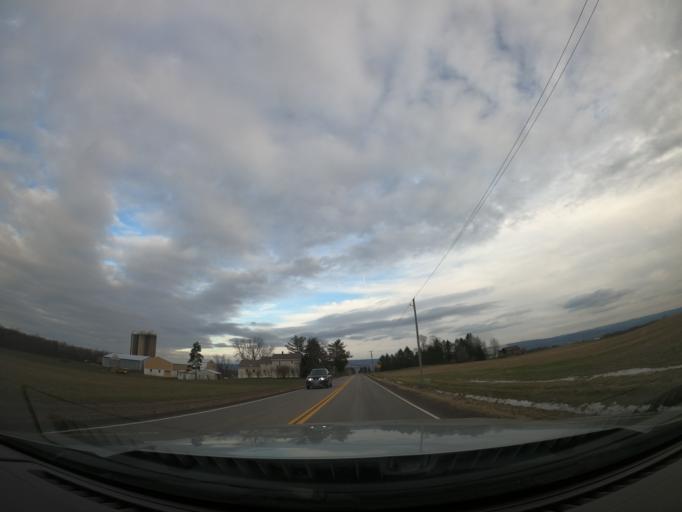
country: US
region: New York
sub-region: Yates County
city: Dundee
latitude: 42.4997
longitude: -76.9443
